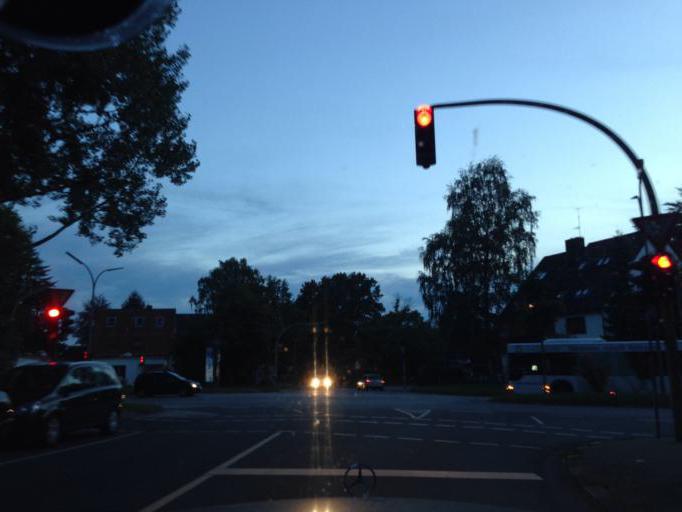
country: DE
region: Hamburg
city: Farmsen-Berne
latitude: 53.6295
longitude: 10.1666
